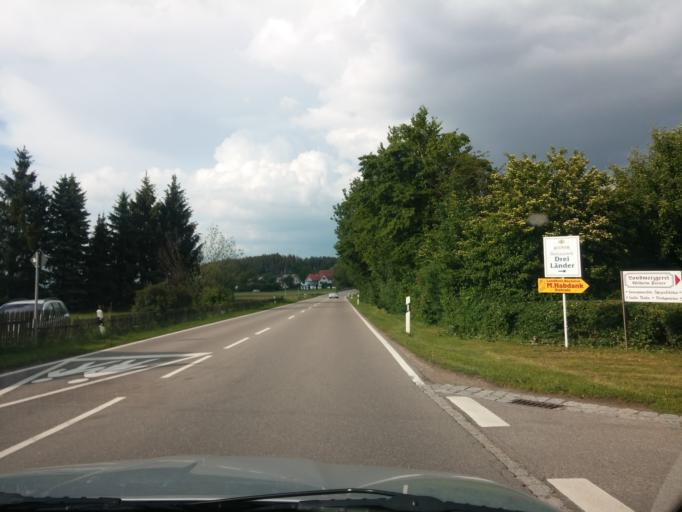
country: DE
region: Baden-Wuerttemberg
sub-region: Tuebingen Region
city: Aitrach
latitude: 47.9537
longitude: 10.1133
